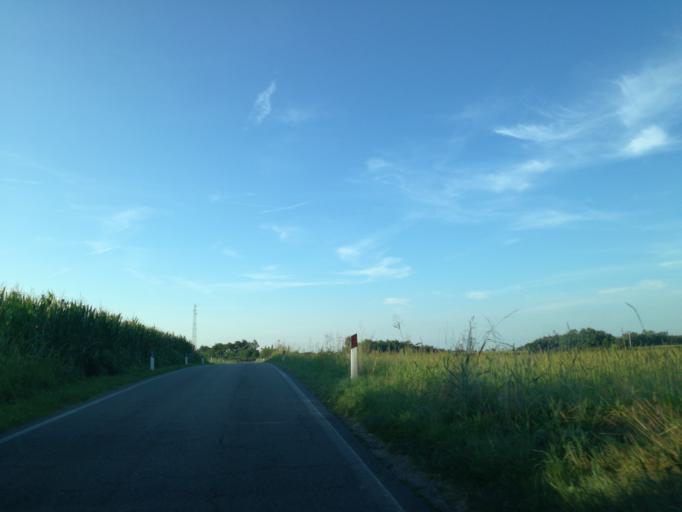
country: IT
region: Lombardy
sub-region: Provincia di Monza e Brianza
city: Sulbiate
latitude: 45.6532
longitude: 9.4296
